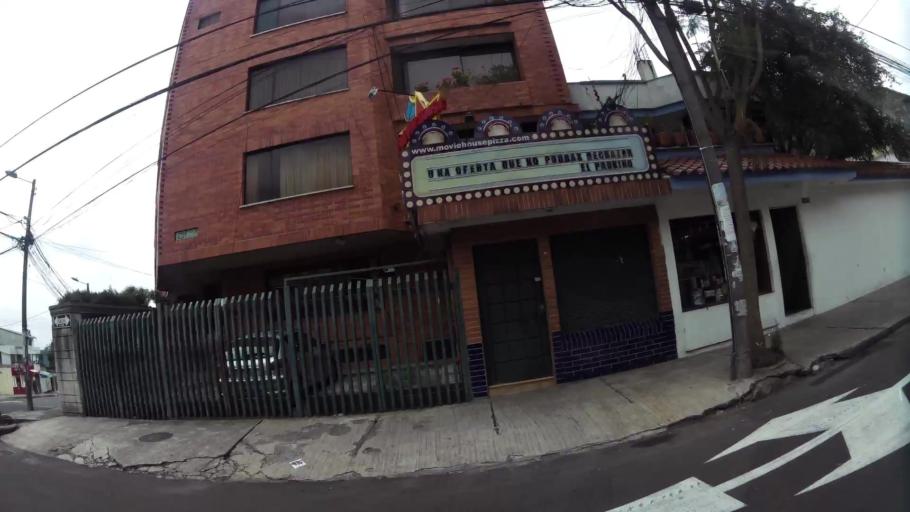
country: EC
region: Pichincha
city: Quito
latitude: -0.1798
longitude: -78.4959
